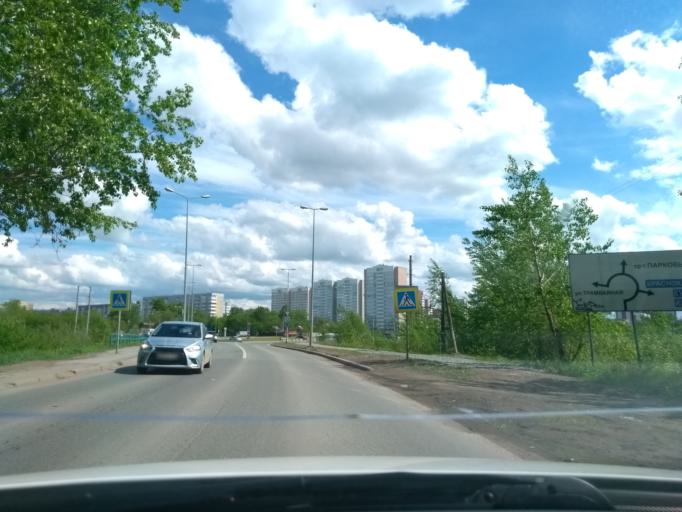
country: RU
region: Perm
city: Kondratovo
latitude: 58.0016
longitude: 56.1309
